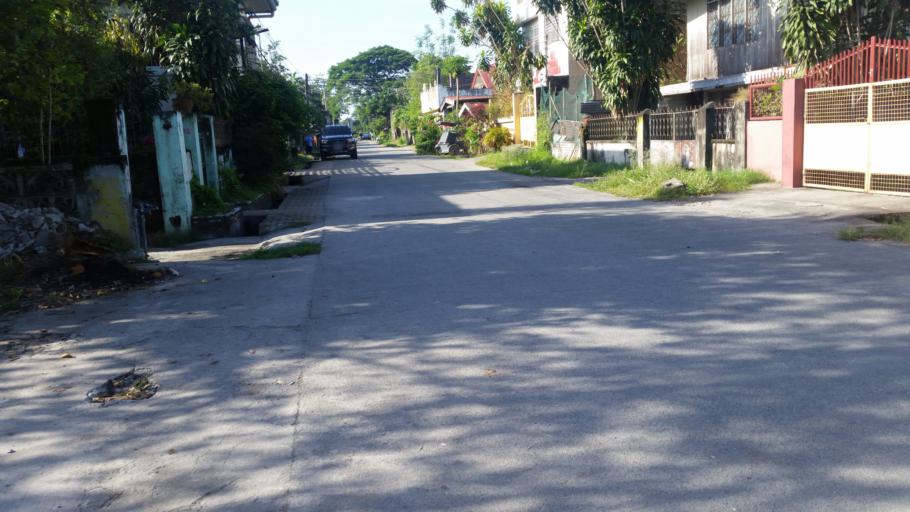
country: PH
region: Central Luzon
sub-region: Province of Pampanga
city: Mabalacat City
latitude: 15.2762
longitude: 120.5683
